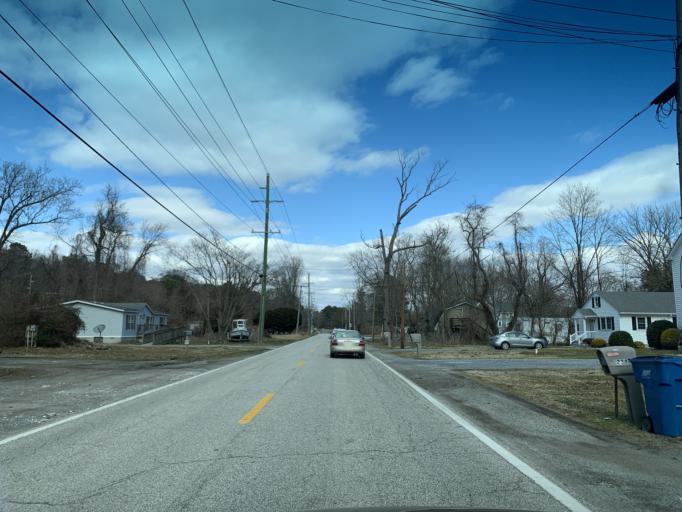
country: US
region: Maryland
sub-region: Queen Anne's County
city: Grasonville
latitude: 38.9787
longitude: -76.1675
